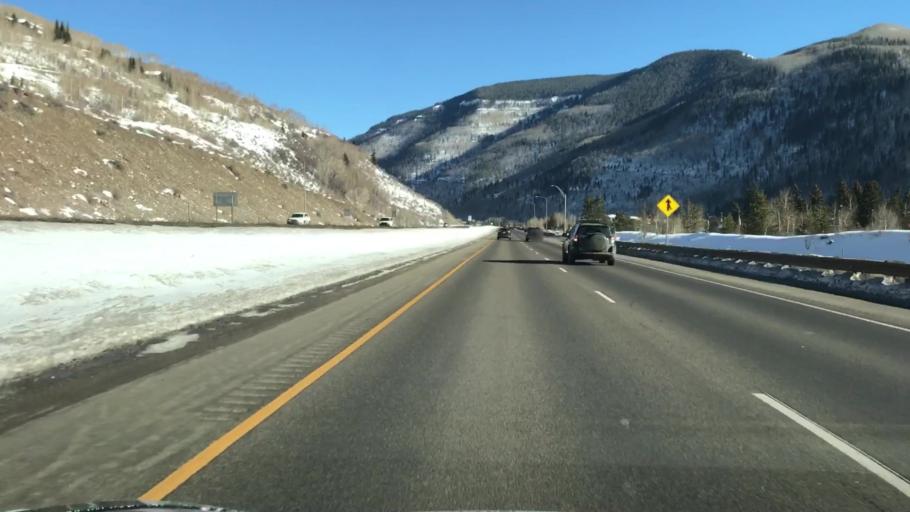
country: US
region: Colorado
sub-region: Eagle County
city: Vail
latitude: 39.6437
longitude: -106.3759
